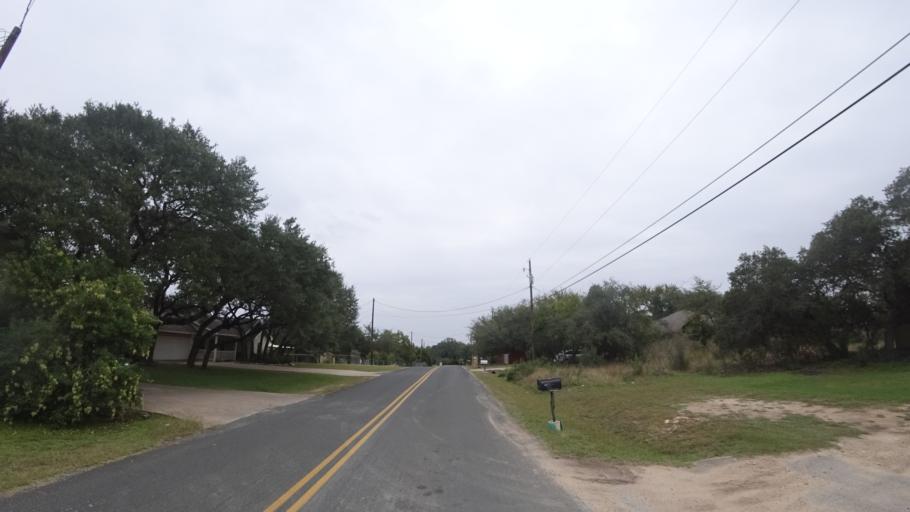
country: US
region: Texas
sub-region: Travis County
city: Lakeway
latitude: 30.3698
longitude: -97.9366
